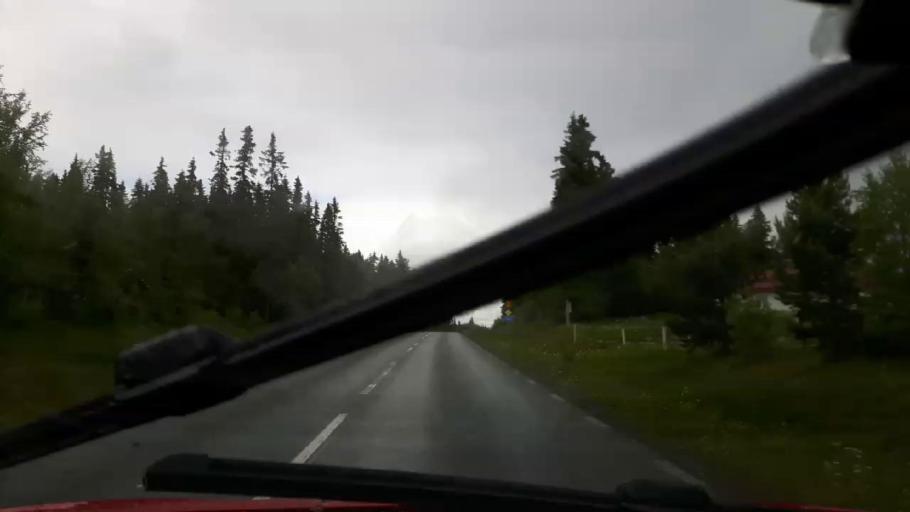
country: SE
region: Jaemtland
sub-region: Krokoms Kommun
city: Krokom
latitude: 63.4581
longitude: 14.1900
